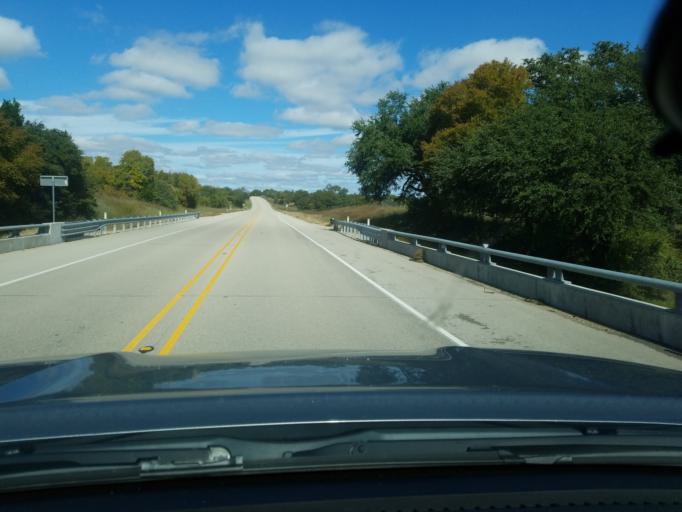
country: US
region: Texas
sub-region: Hamilton County
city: Hamilton
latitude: 31.5822
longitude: -98.1571
